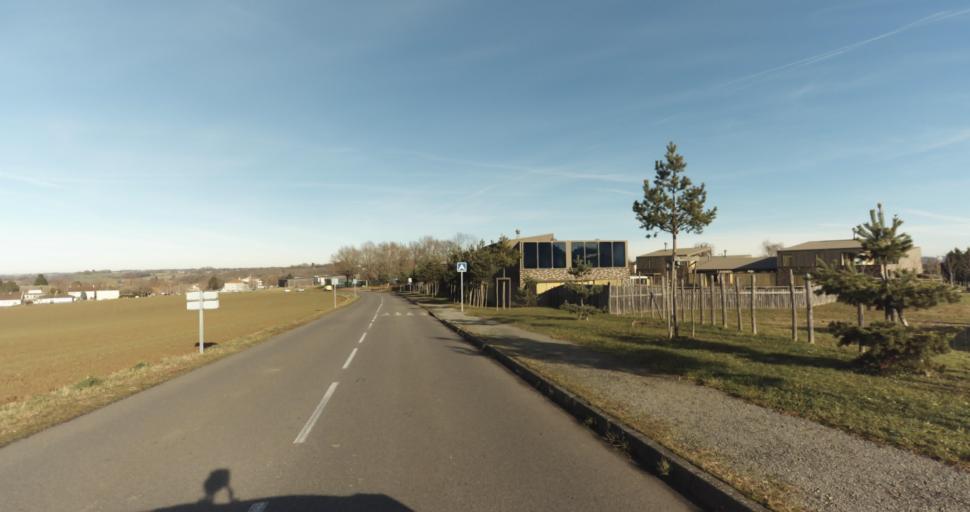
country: FR
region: Limousin
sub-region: Departement de la Haute-Vienne
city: Aixe-sur-Vienne
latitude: 45.7894
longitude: 1.1295
